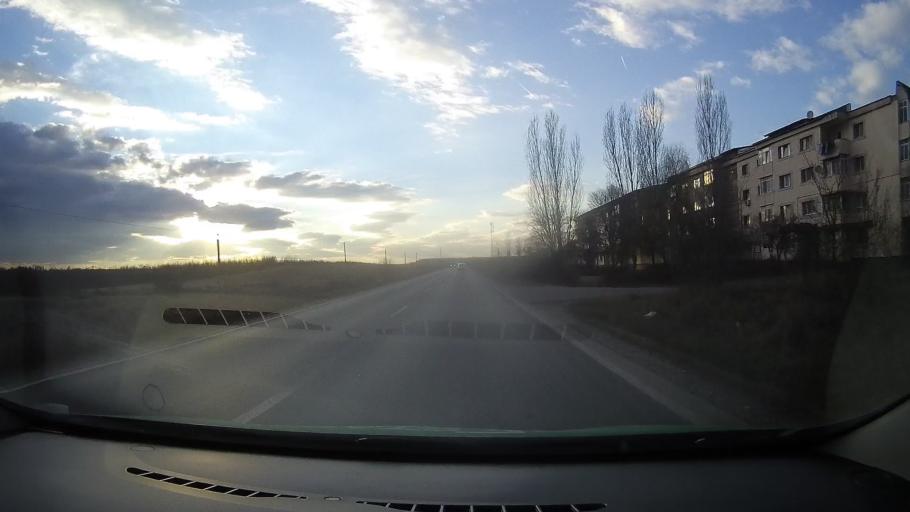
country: RO
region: Dambovita
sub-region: Comuna I. L. Caragiale
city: Mija
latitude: 44.9123
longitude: 25.6781
